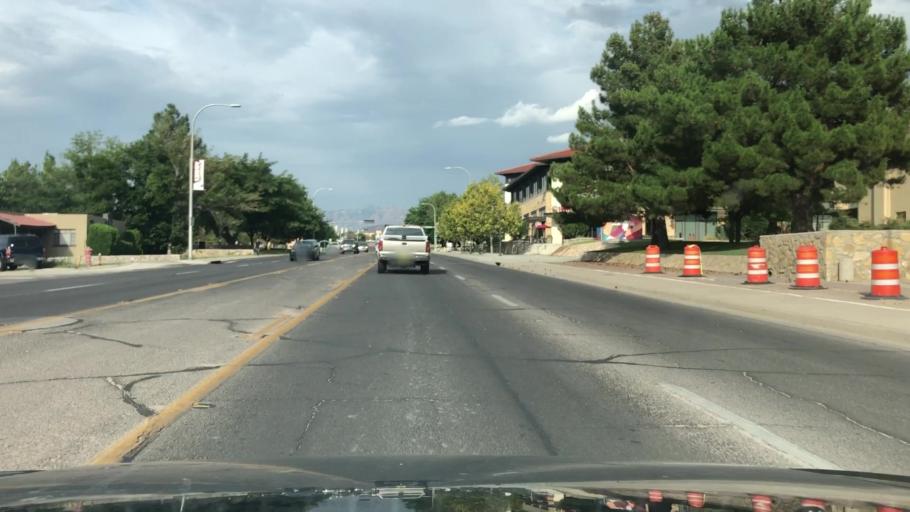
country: US
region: New Mexico
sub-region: Dona Ana County
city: University Park
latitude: 32.2849
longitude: -106.7516
